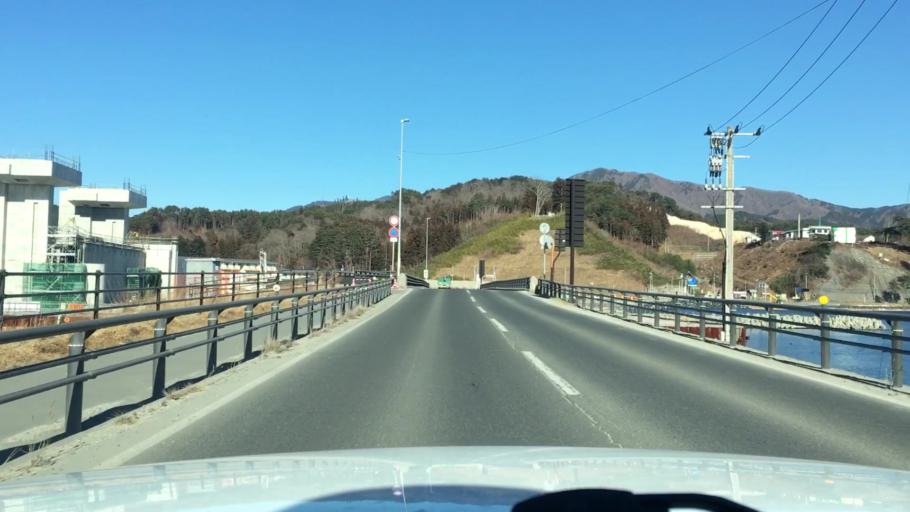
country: JP
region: Iwate
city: Yamada
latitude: 39.4731
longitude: 141.9545
